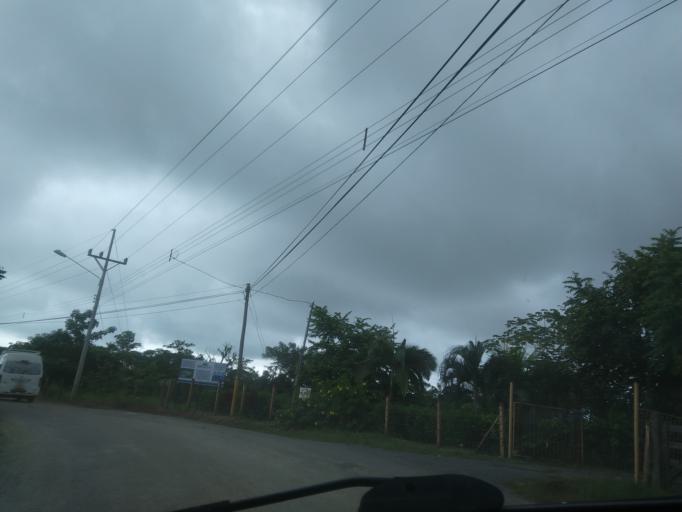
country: CR
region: Puntarenas
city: Paquera
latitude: 9.6500
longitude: -85.1363
